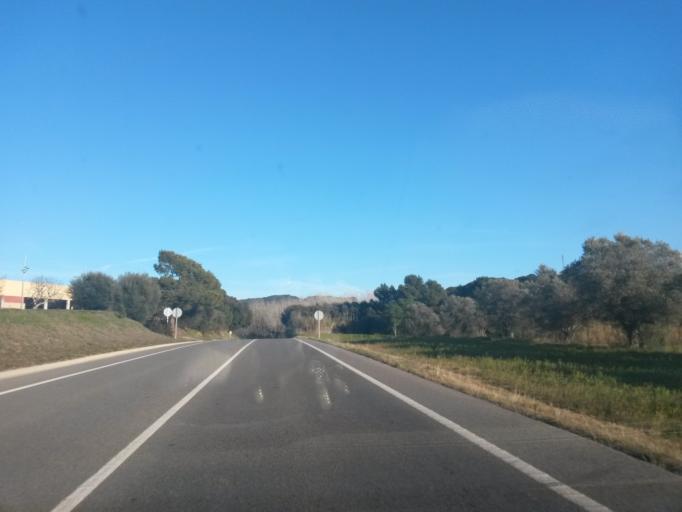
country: ES
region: Catalonia
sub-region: Provincia de Girona
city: Regencos
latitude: 41.9514
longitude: 3.1718
